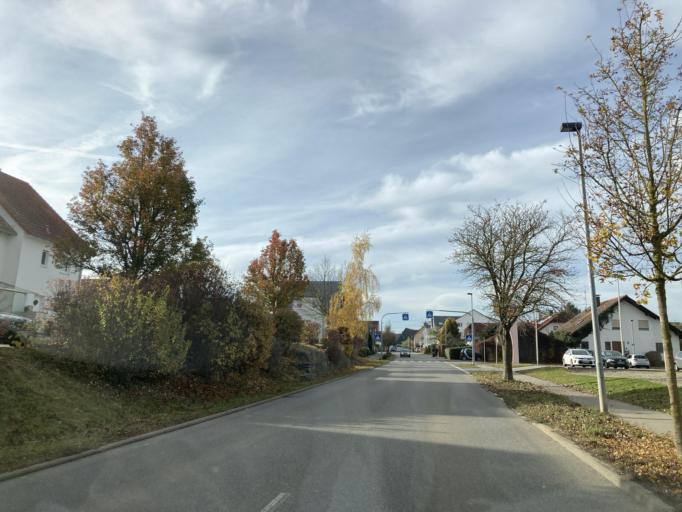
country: DE
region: Baden-Wuerttemberg
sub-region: Regierungsbezirk Stuttgart
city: Bondorf
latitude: 48.5227
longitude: 8.8407
